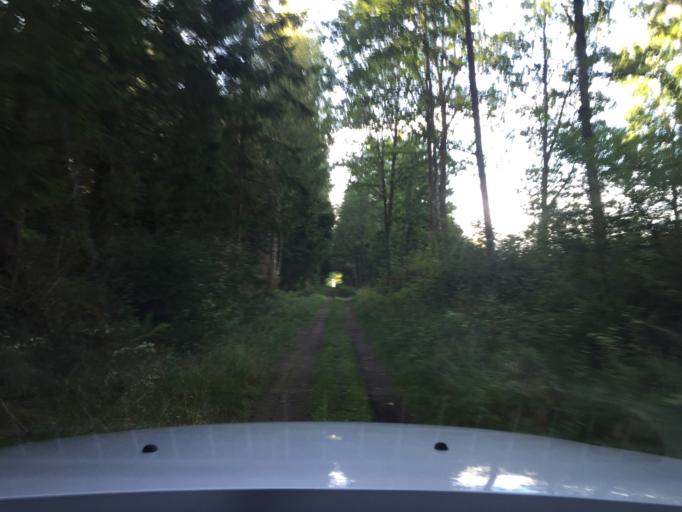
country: SE
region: Skane
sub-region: Hassleholms Kommun
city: Sosdala
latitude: 56.0192
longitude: 13.7140
